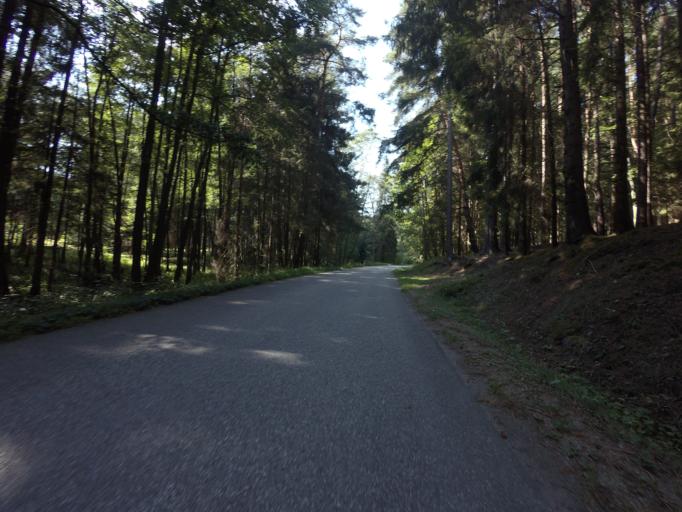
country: CZ
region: Jihocesky
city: Tyn nad Vltavou
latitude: 49.1577
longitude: 14.4307
